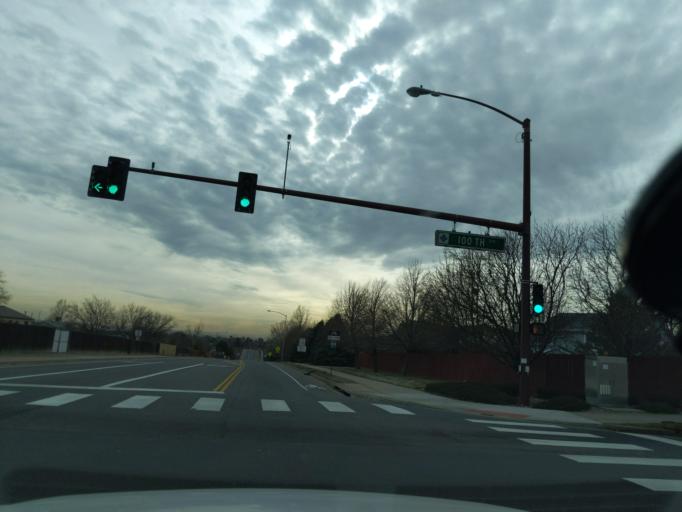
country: US
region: Colorado
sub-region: Adams County
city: Thornton
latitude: 39.8779
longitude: -104.9590
